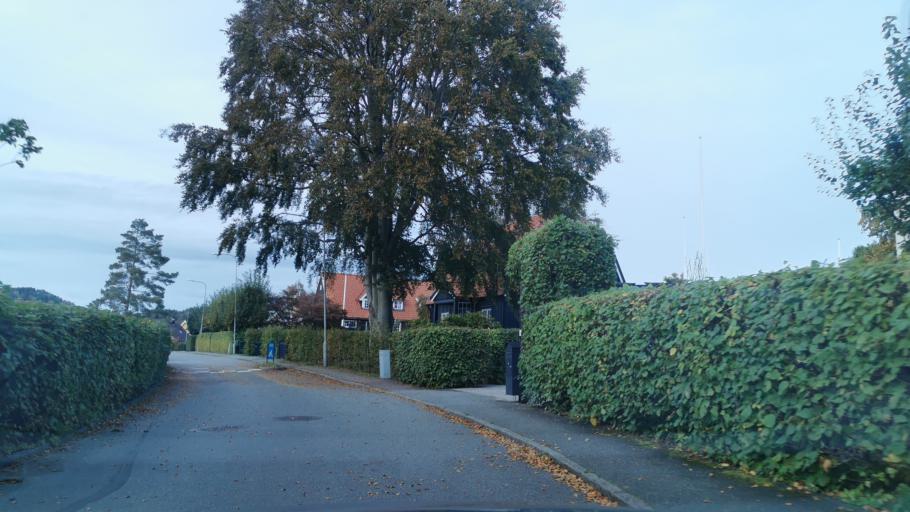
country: SE
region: Vaestra Goetaland
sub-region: Goteborg
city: Eriksbo
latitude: 57.7375
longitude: 12.0445
